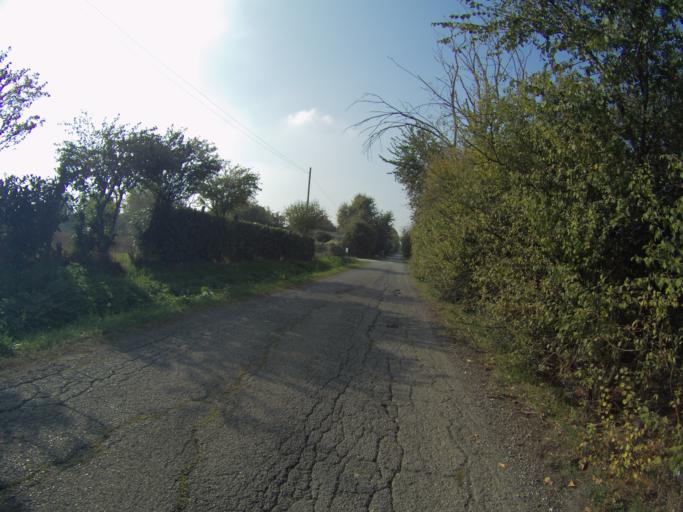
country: IT
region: Emilia-Romagna
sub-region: Provincia di Reggio Emilia
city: Forche
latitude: 44.6536
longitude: 10.5628
